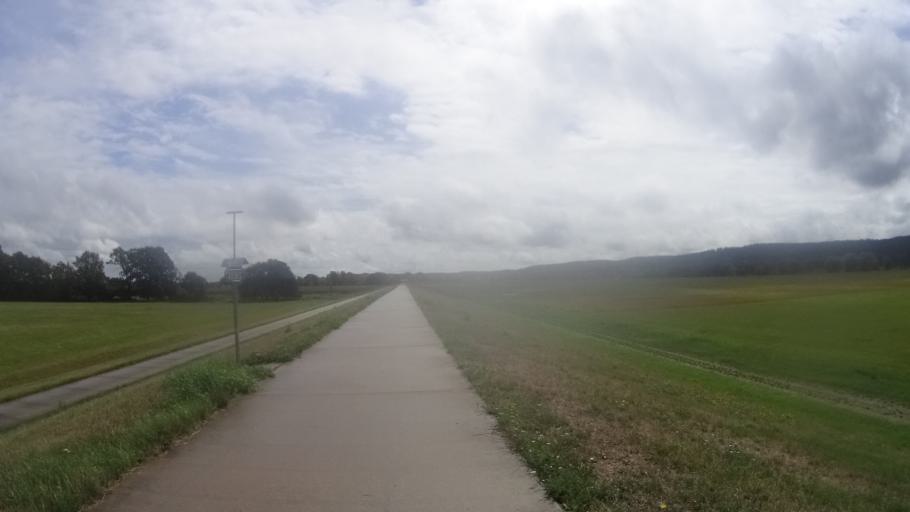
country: DE
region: Lower Saxony
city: Neu Darchau
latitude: 53.2313
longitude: 10.9283
